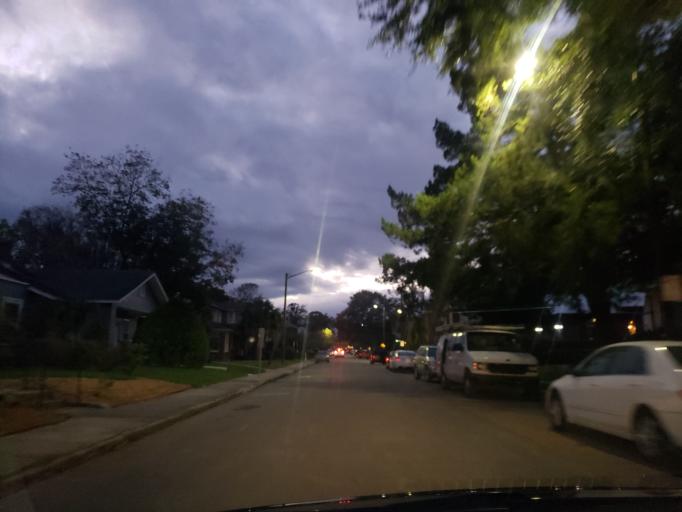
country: US
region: Georgia
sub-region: Chatham County
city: Savannah
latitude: 32.0512
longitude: -81.0901
